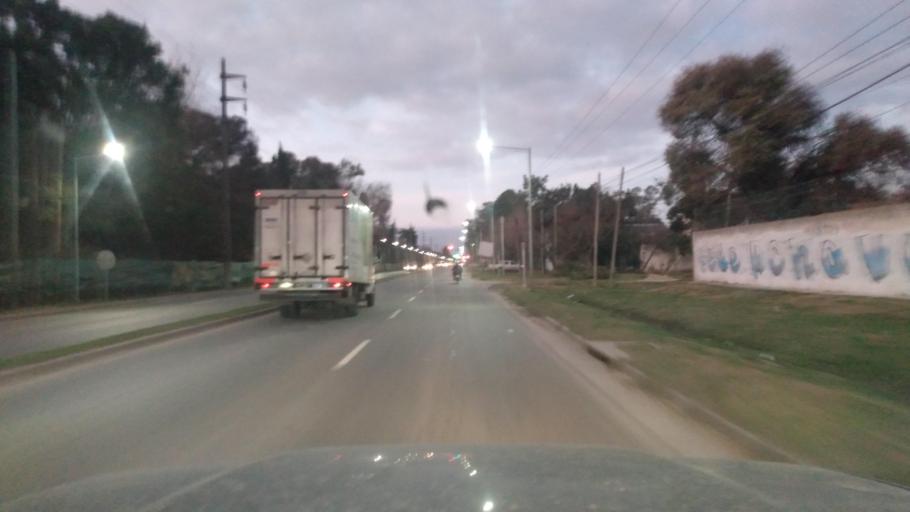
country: AR
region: Buenos Aires
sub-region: Partido de Pilar
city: Pilar
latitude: -34.4410
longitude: -58.8978
